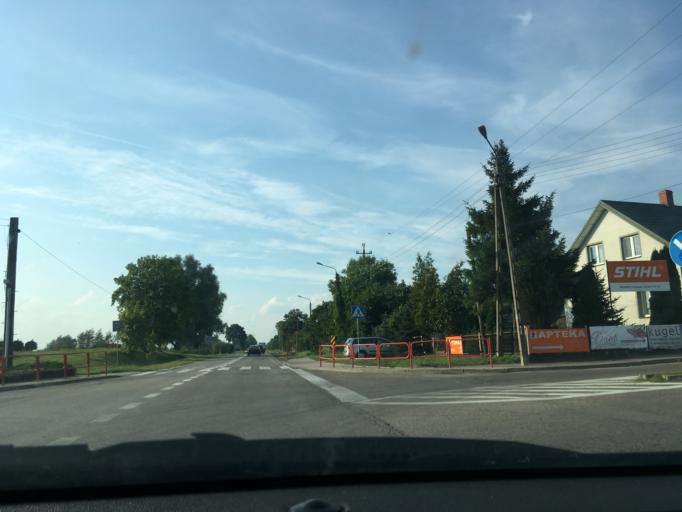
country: PL
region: Podlasie
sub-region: Powiat moniecki
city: Knyszyn
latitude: 53.3086
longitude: 22.9138
